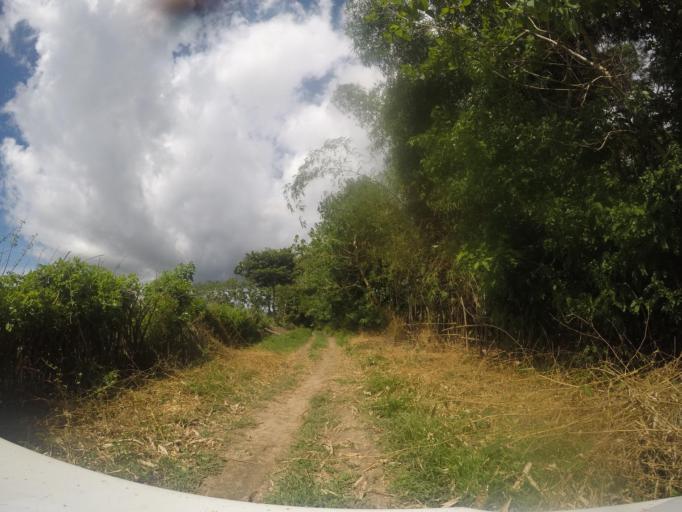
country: TL
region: Lautem
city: Lospalos
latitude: -8.4956
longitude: 126.9999
